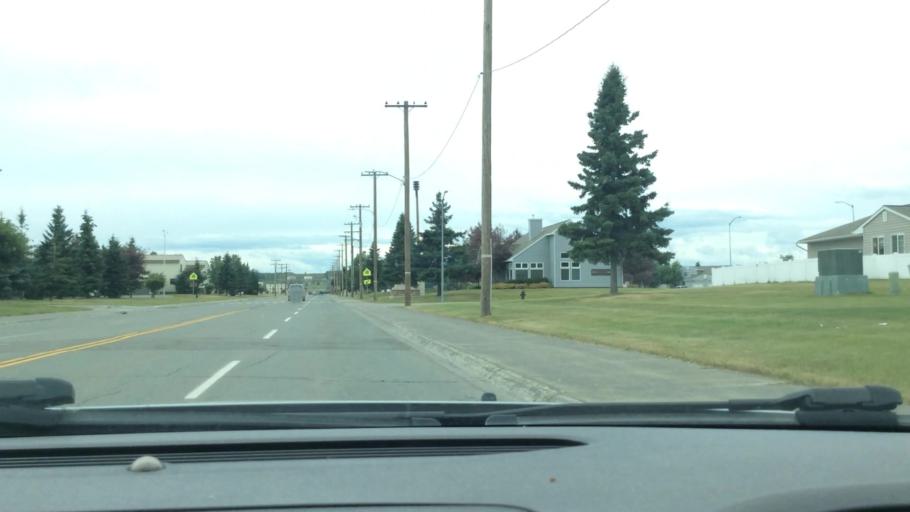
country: US
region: Alaska
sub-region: Anchorage Municipality
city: Anchorage
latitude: 61.2322
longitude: -149.8491
